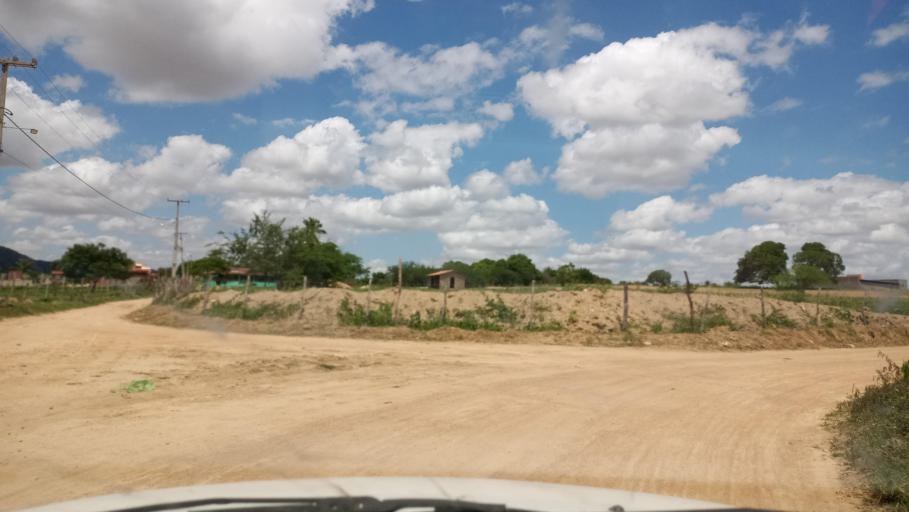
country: BR
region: Rio Grande do Norte
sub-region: Sao Jose Do Campestre
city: Sao Jose do Campestre
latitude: -6.4405
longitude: -35.6326
